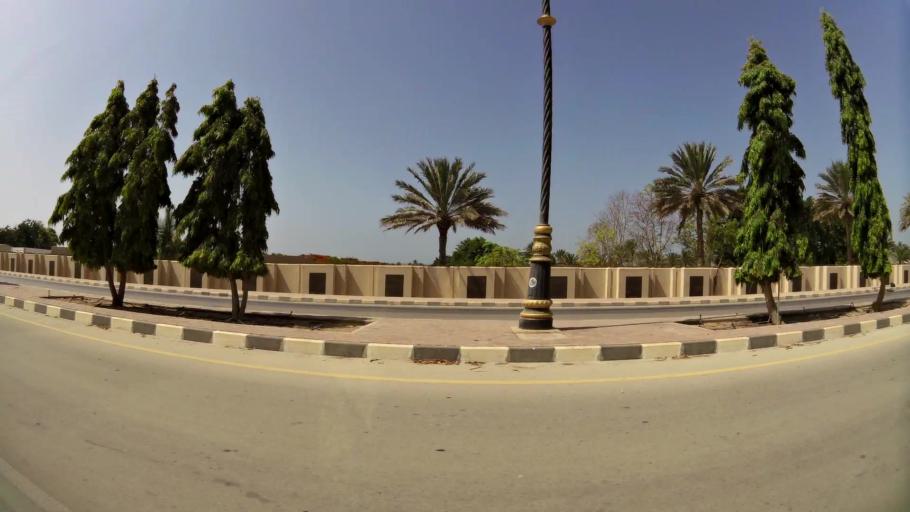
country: OM
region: Zufar
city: Salalah
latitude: 17.0262
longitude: 54.1485
